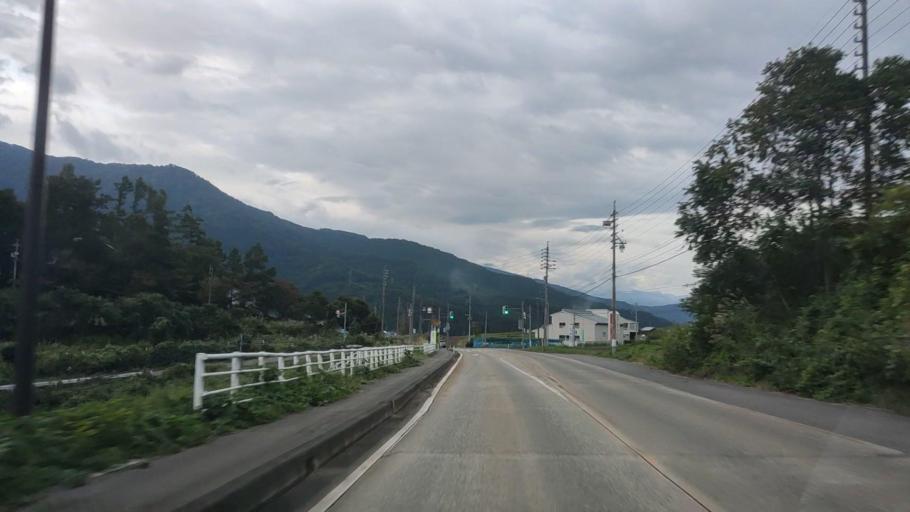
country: JP
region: Nagano
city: Iiyama
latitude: 36.8872
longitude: 138.4097
